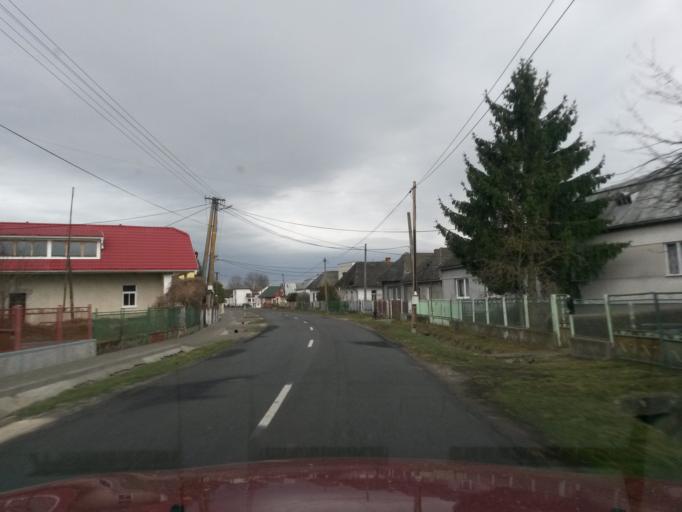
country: SK
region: Kosicky
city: Michalovce
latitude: 48.6643
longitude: 22.0242
